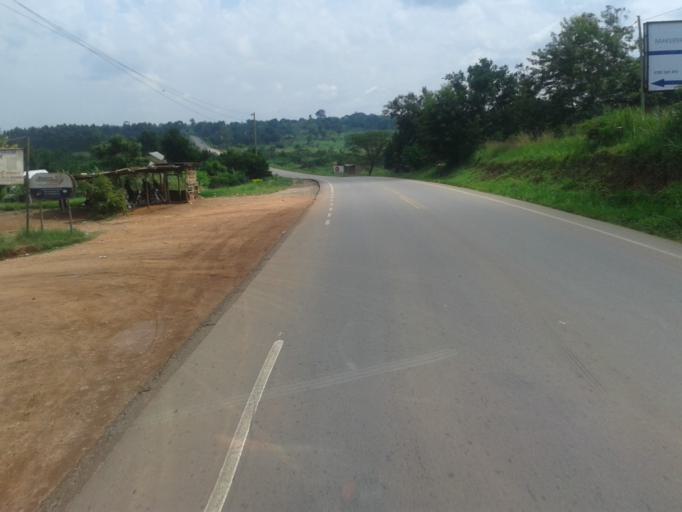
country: UG
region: Central Region
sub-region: Wakiso District
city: Wakiso
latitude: 0.5414
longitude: 32.5330
